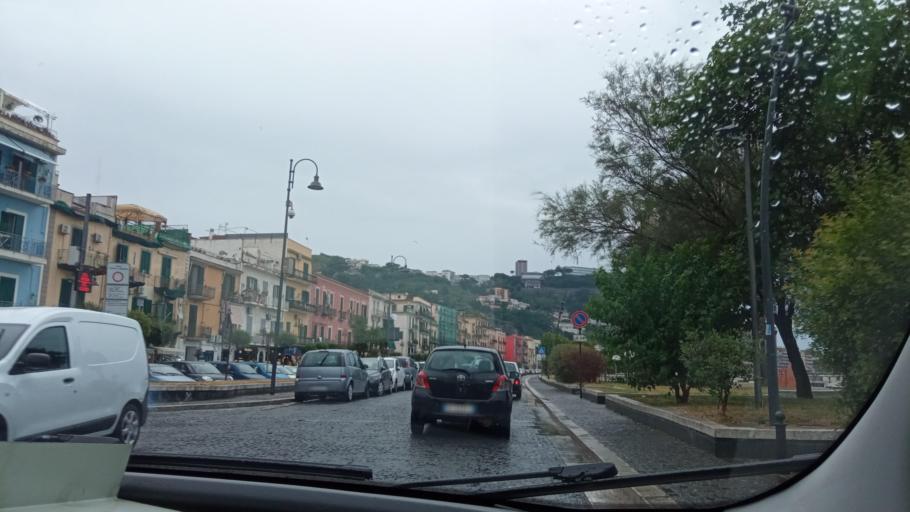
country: IT
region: Campania
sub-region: Provincia di Napoli
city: Pozzuoli
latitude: 40.8212
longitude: 14.1260
